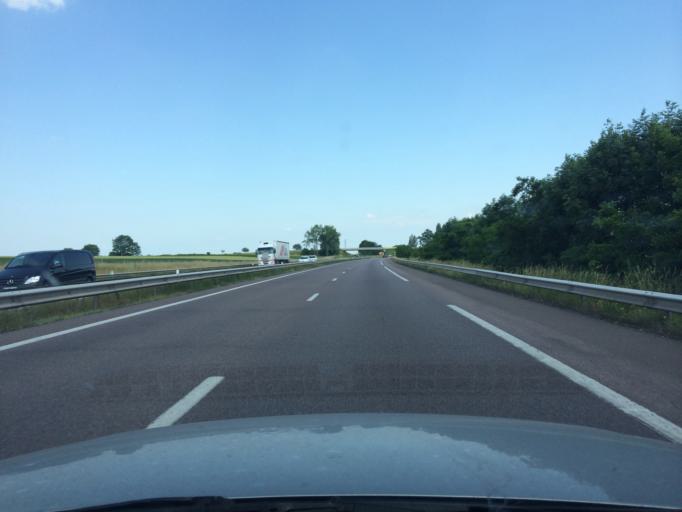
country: FR
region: Alsace
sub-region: Departement du Bas-Rhin
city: Hochfelden
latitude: 48.7698
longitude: 7.5285
